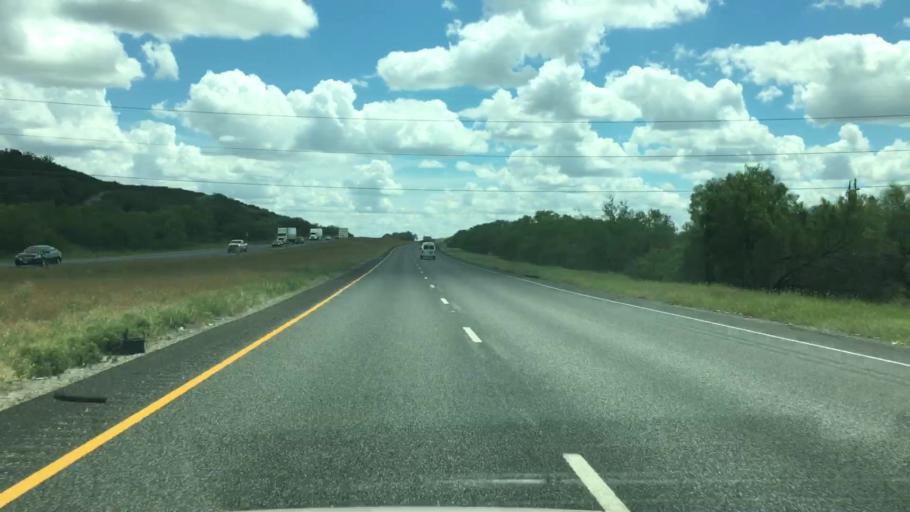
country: US
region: Texas
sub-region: Live Oak County
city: Three Rivers
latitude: 28.7262
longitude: -98.2870
